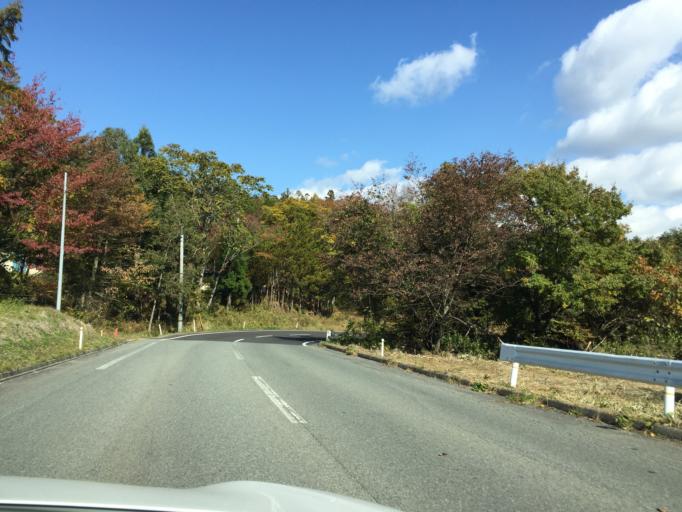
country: JP
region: Fukushima
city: Funehikimachi-funehiki
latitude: 37.3048
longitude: 140.7628
